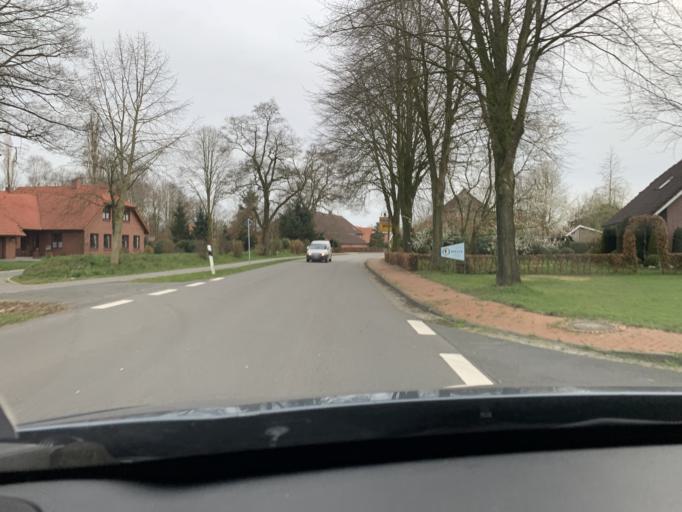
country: DE
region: Lower Saxony
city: Detern
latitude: 53.2567
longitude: 7.7110
